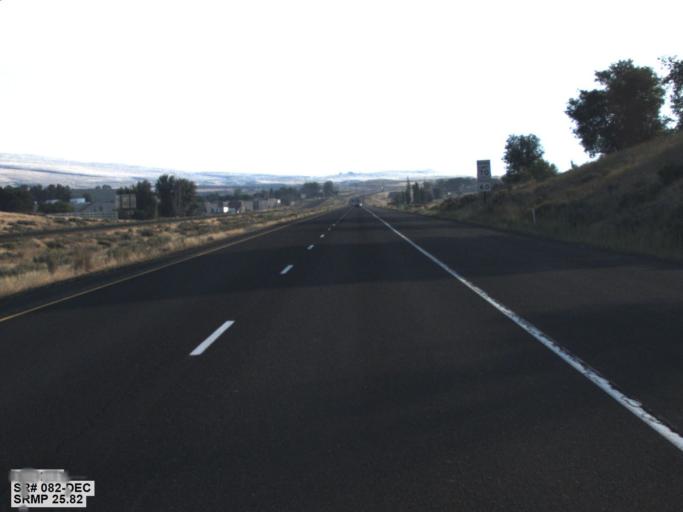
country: US
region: Washington
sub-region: Yakima County
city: Selah
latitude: 46.6843
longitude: -120.4687
